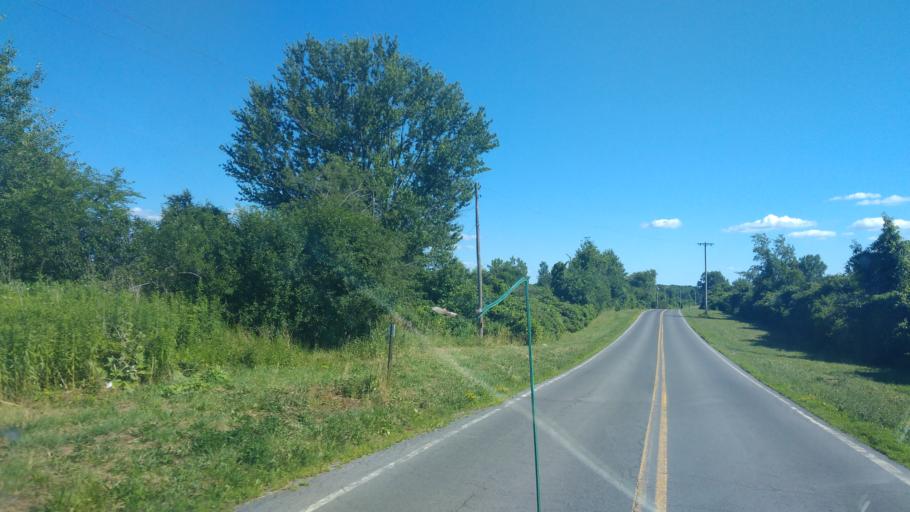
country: US
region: New York
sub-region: Seneca County
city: Seneca Falls
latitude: 43.0008
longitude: -76.8078
